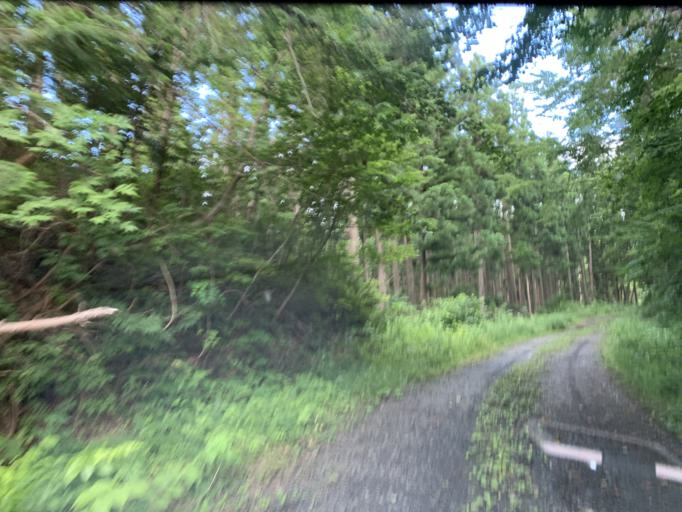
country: JP
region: Iwate
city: Ichinoseki
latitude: 38.9052
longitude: 140.9515
